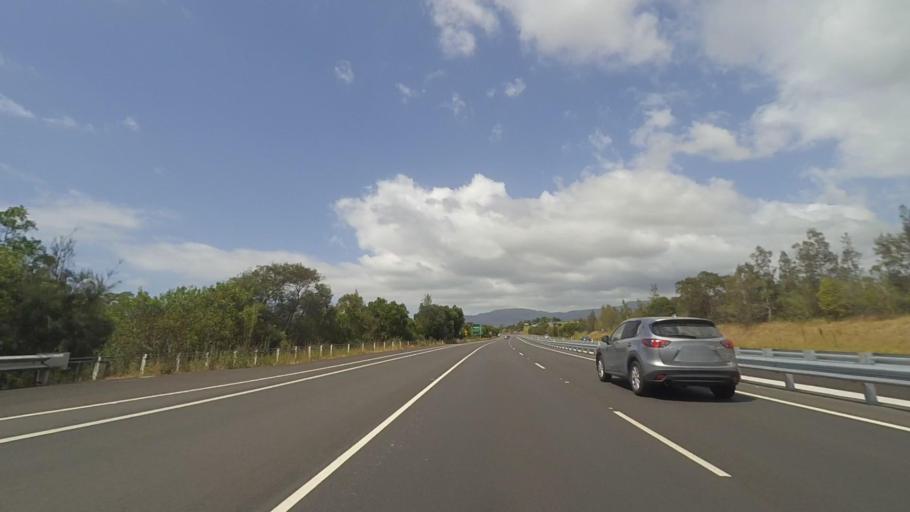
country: AU
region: New South Wales
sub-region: Shellharbour
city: Croom
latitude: -34.6312
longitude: 150.8349
